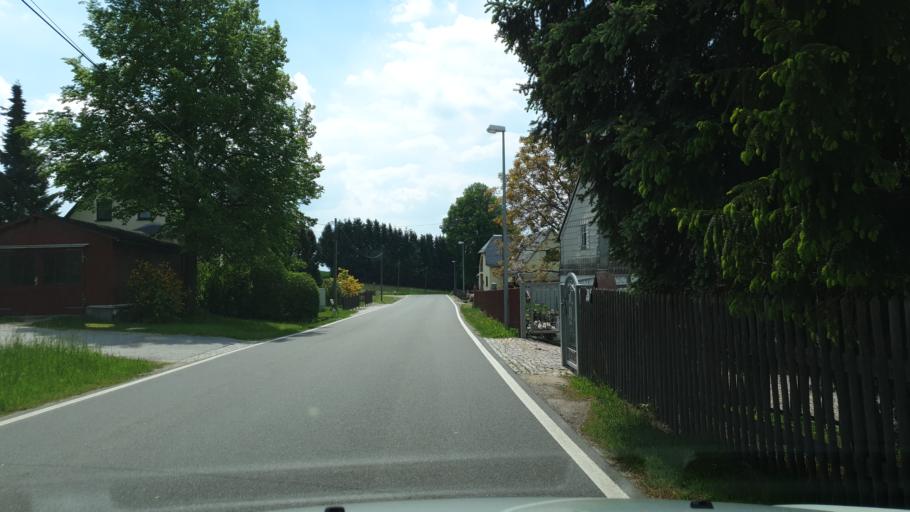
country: DE
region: Saxony
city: Hartenstein
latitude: 50.6843
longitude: 12.6978
